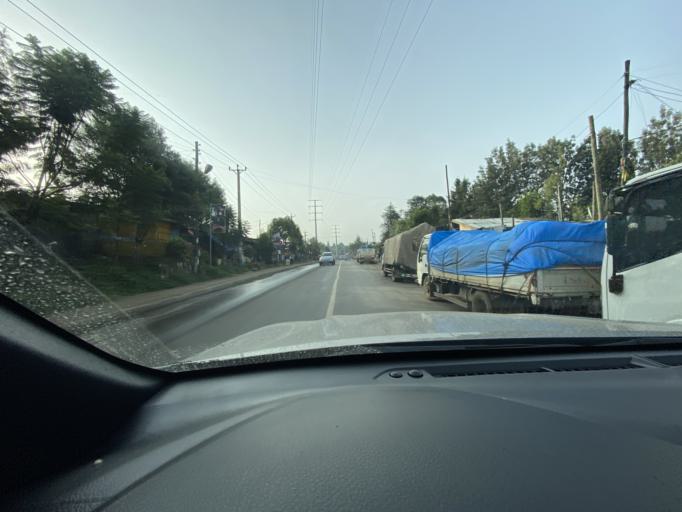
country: ET
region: Adis Abeba
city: Addis Ababa
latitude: 9.0177
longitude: 38.7281
